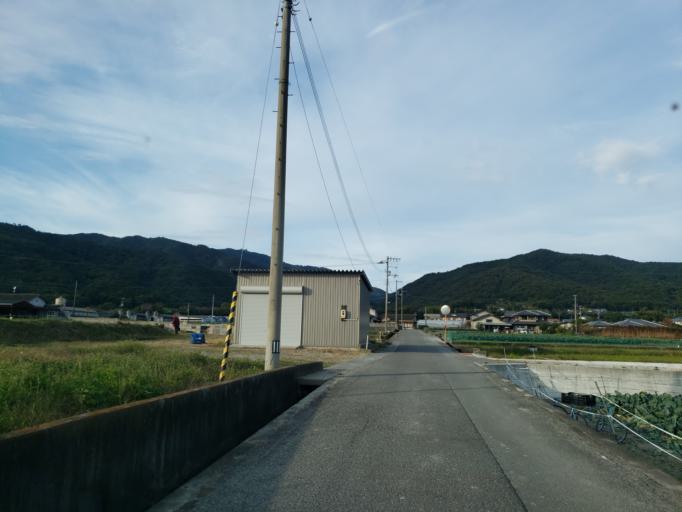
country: JP
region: Tokushima
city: Wakimachi
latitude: 34.0940
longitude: 134.2255
